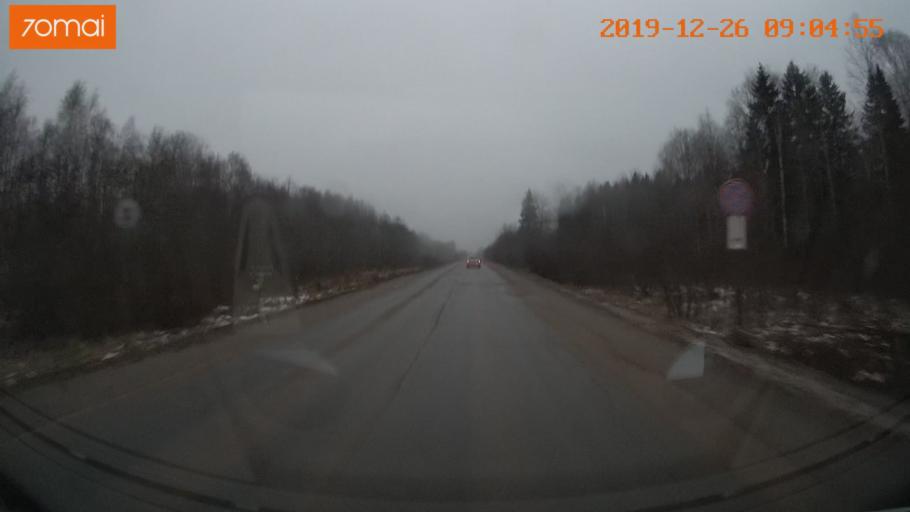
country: RU
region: Vologda
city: Gryazovets
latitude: 58.8199
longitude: 40.2607
